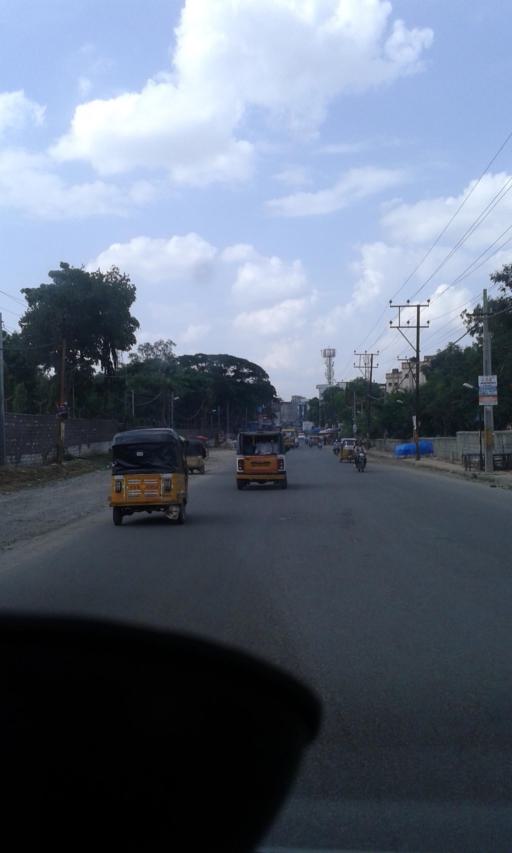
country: IN
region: Telangana
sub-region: Rangareddi
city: Balapur
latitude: 17.3188
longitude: 78.4798
